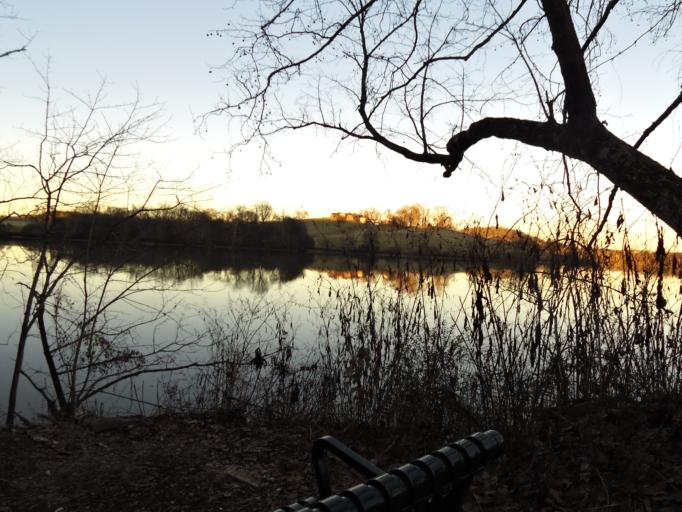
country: US
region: Tennessee
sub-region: Knox County
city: Knoxville
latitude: 35.9552
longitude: -83.8624
